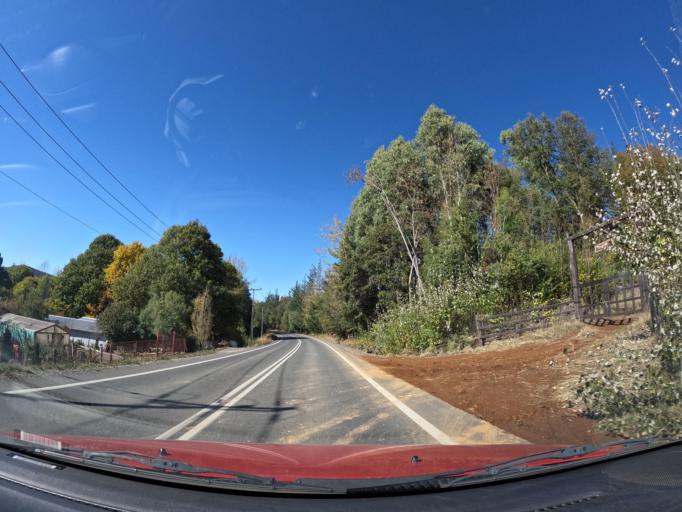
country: CL
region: Biobio
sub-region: Provincia de Nuble
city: Coihueco
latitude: -36.8244
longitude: -71.6943
